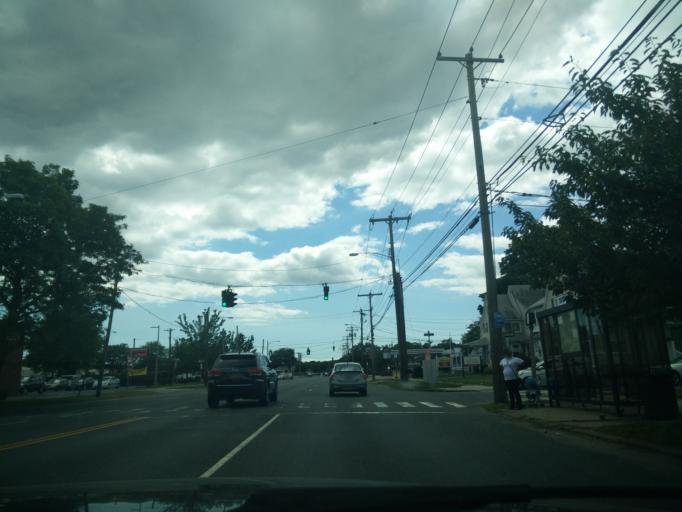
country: US
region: Connecticut
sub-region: New Haven County
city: New Haven
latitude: 41.3493
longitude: -72.9325
